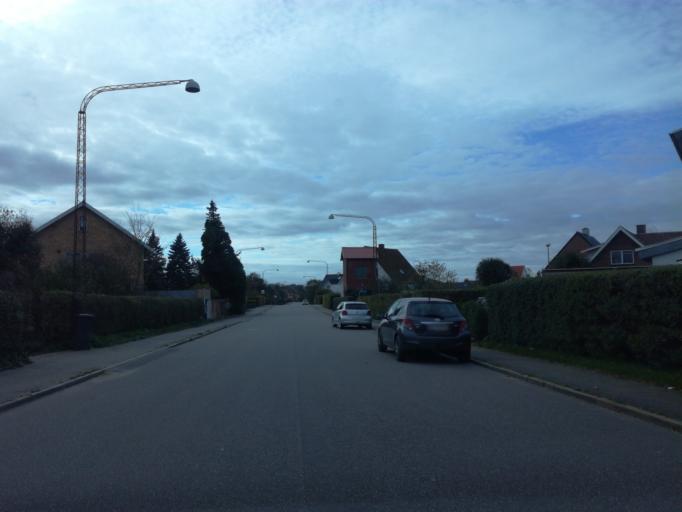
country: DK
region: South Denmark
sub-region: Fredericia Kommune
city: Fredericia
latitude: 55.5764
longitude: 9.7762
